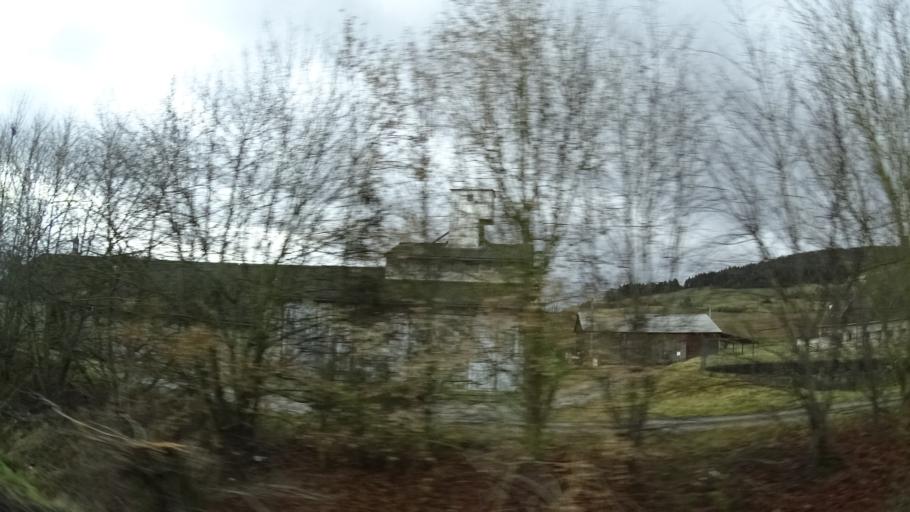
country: DE
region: Thuringia
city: Rippershausen
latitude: 50.5798
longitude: 10.3298
